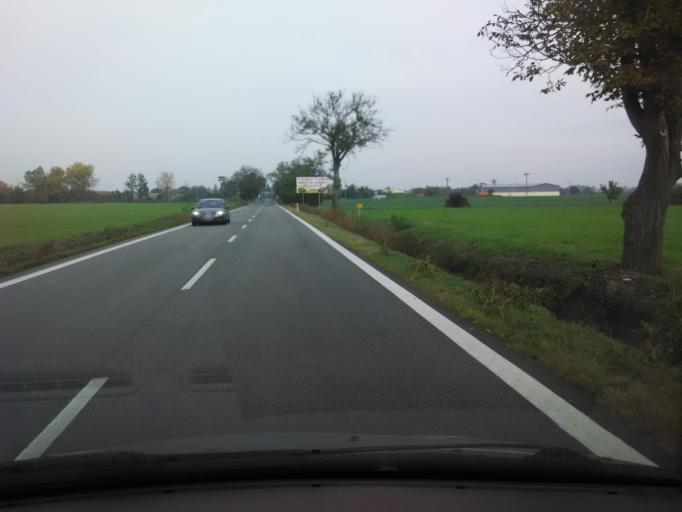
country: SK
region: Nitriansky
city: Zeliezovce
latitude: 48.0877
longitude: 18.5390
